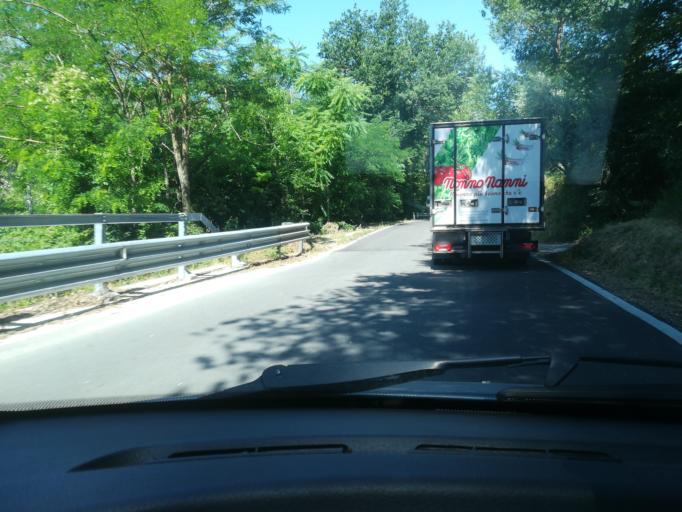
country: IT
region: The Marches
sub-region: Provincia di Macerata
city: Ripe San Ginesio
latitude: 43.1136
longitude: 13.3613
